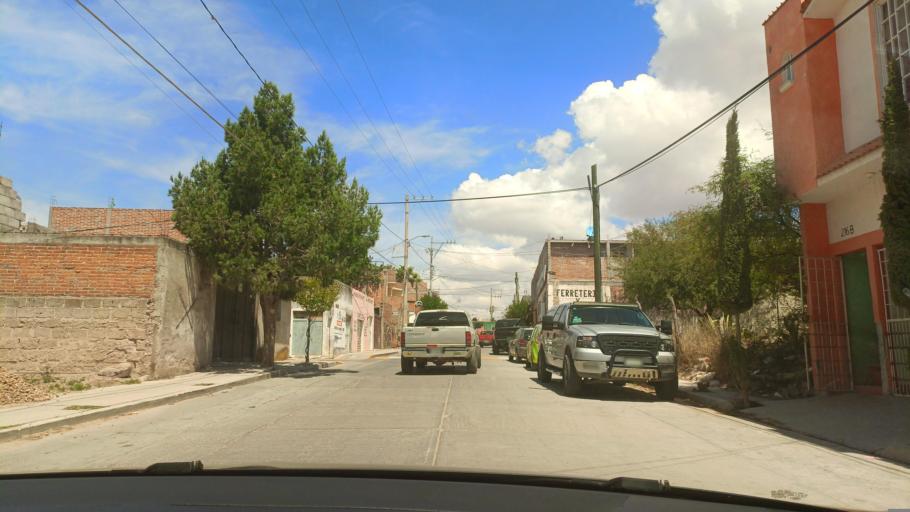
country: MX
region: Guanajuato
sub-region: San Luis de la Paz
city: San Luis de la Paz
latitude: 21.3022
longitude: -100.5080
